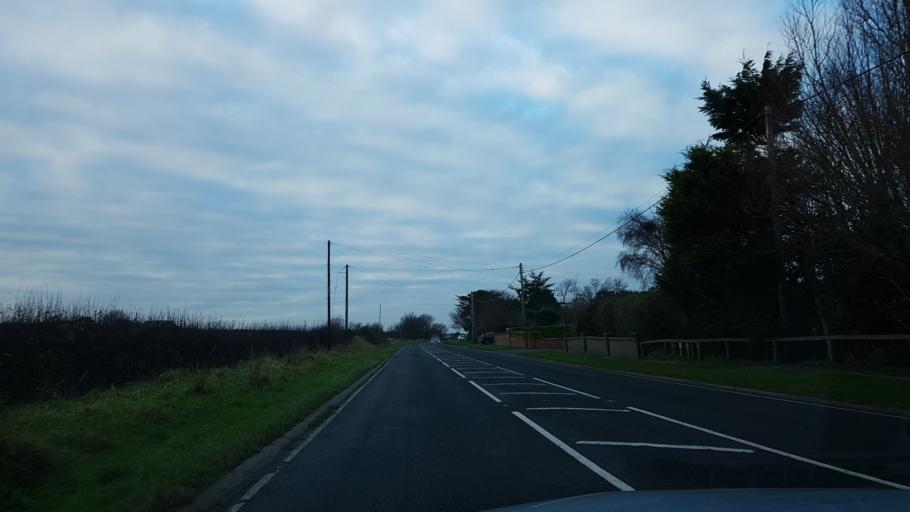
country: GB
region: Northern Ireland
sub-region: Down District
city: Donaghadee
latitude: 54.6721
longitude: -5.5995
